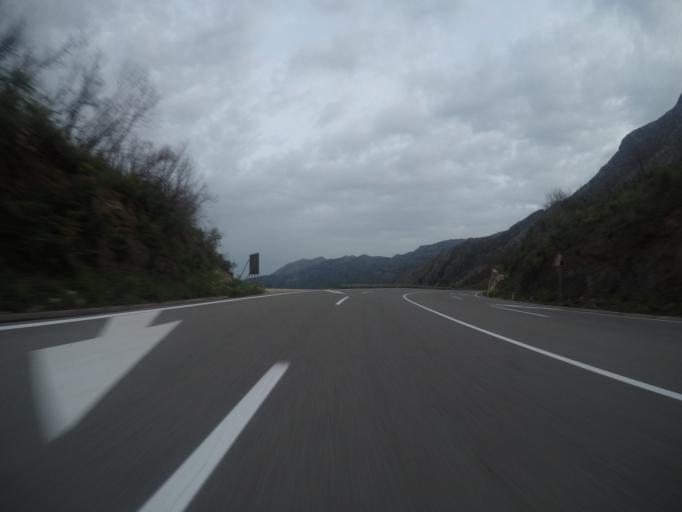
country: ME
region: Bar
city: Sutomore
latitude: 42.1756
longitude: 18.9975
